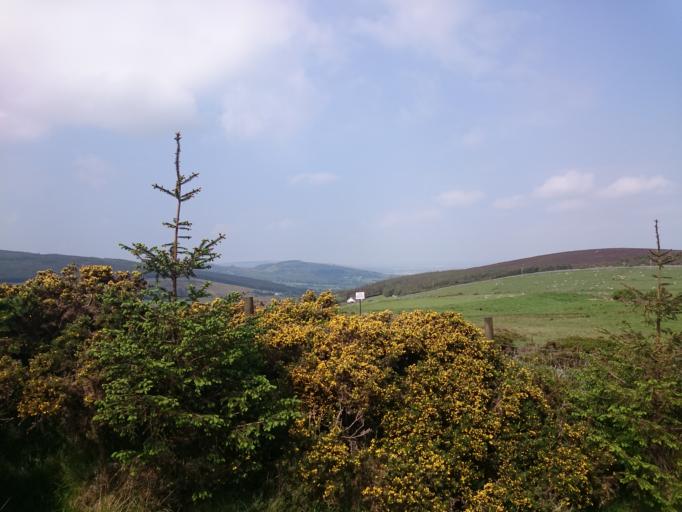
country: IE
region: Leinster
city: Ballinteer
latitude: 53.2460
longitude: -6.2580
